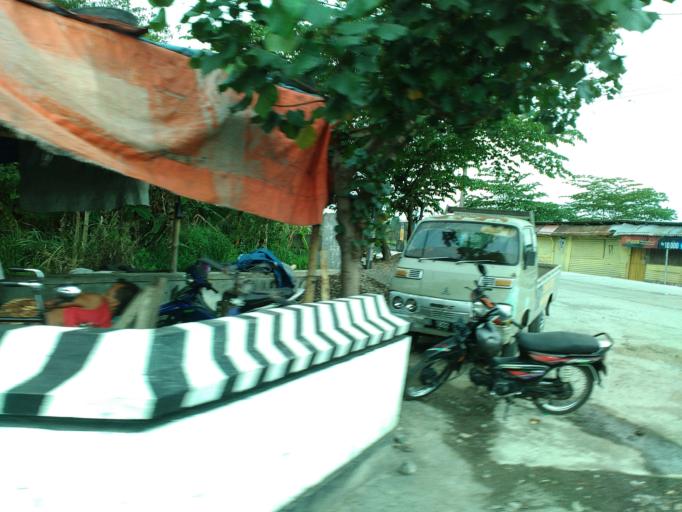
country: ID
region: Central Java
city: Delanggu
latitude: -7.6109
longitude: 110.7012
